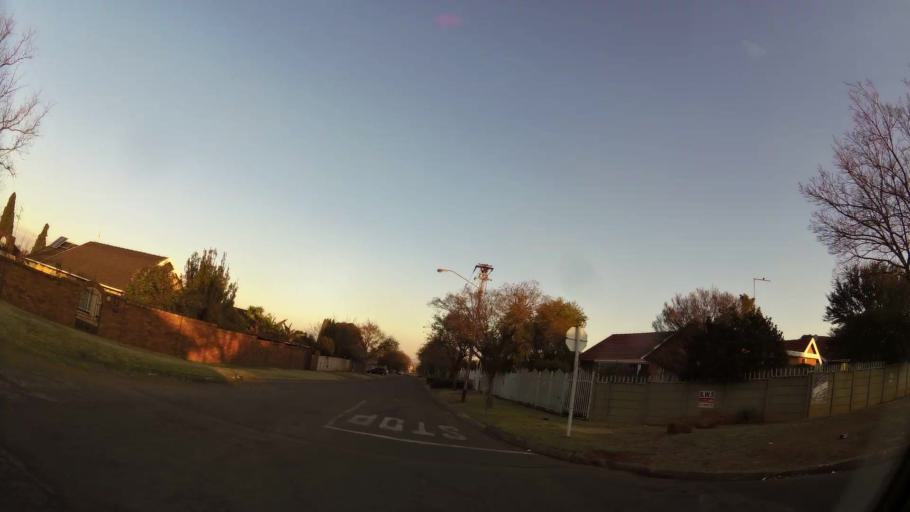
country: ZA
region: Gauteng
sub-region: Ekurhuleni Metropolitan Municipality
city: Germiston
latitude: -26.2598
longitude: 28.1624
